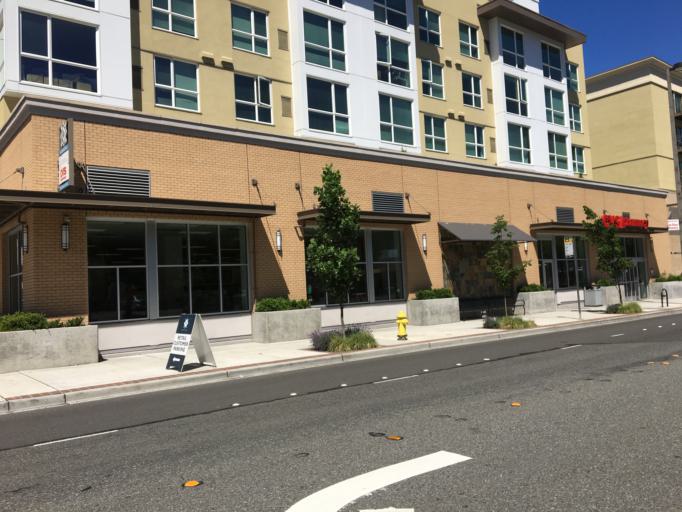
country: US
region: Washington
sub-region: King County
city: Bellevue
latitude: 47.6092
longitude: -122.2015
